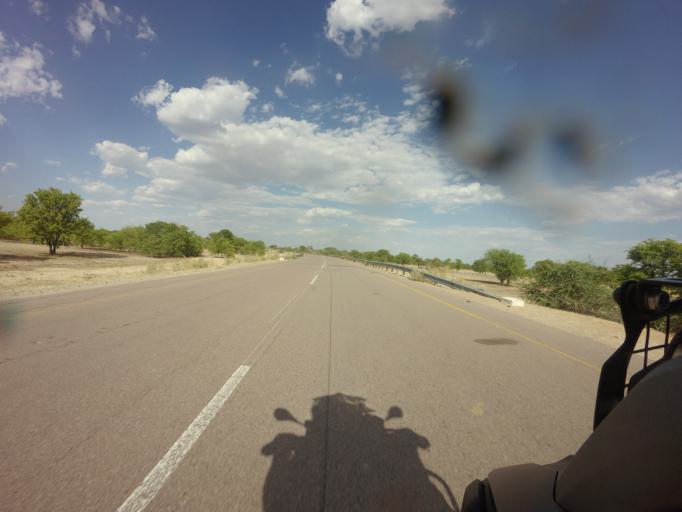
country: AO
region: Cunene
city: Ondjiva
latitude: -16.7273
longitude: 15.2421
